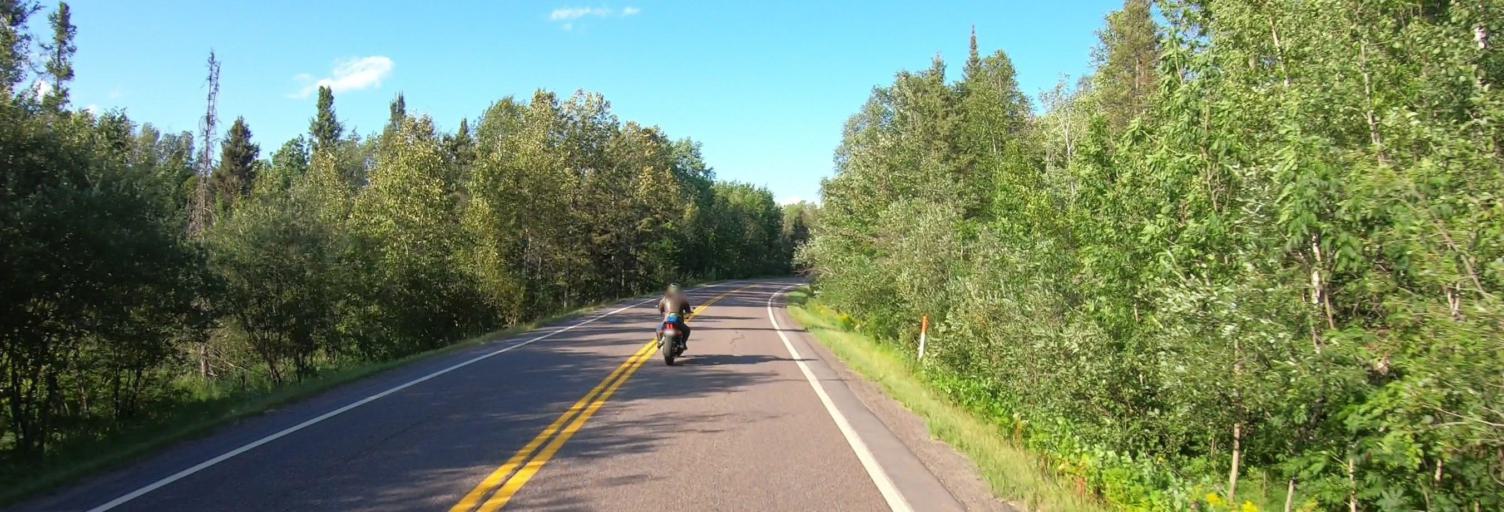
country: US
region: Minnesota
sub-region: Saint Louis County
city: Ely
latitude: 47.9507
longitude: -91.6465
